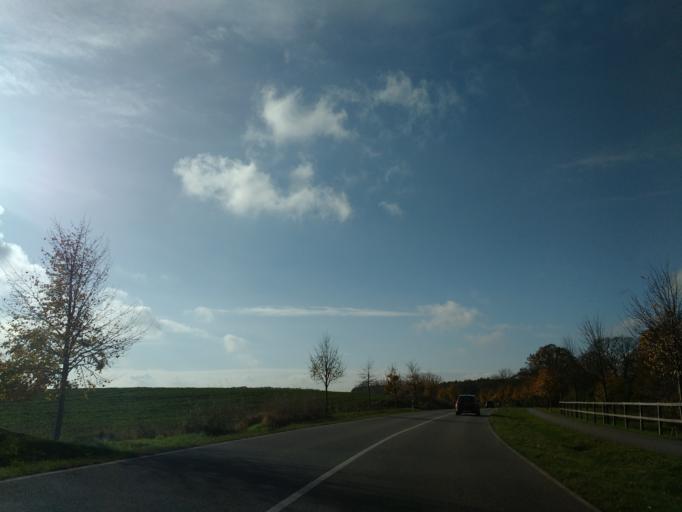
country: DE
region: Mecklenburg-Vorpommern
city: Ostseebad Boltenhagen
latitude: 53.9600
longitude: 11.2272
